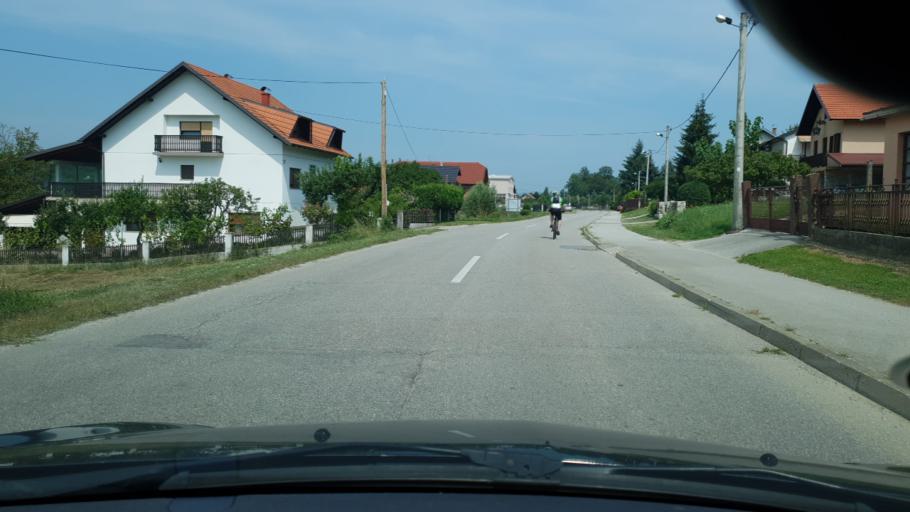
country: HR
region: Krapinsko-Zagorska
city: Marija Bistrica
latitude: 46.0098
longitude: 16.1100
